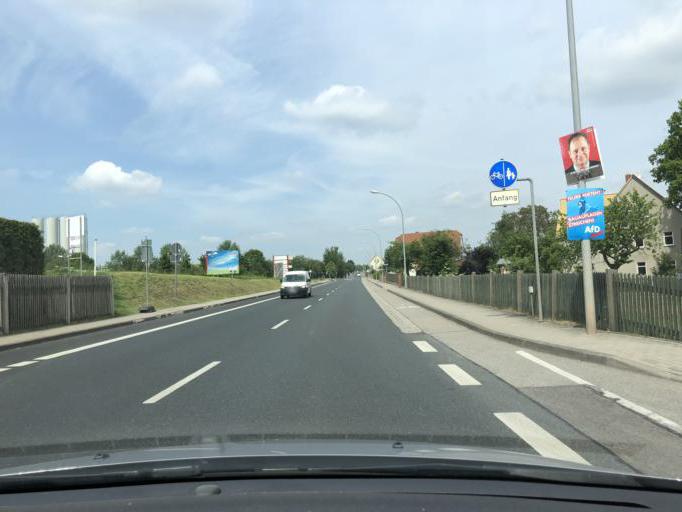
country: DE
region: Thuringia
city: Saara
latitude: 50.9507
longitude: 12.4261
